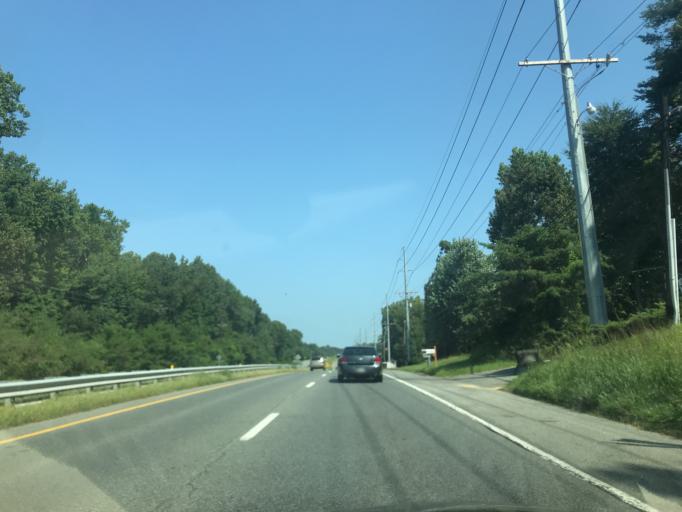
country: US
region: Maryland
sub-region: Calvert County
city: Huntingtown Town Center
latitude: 38.6363
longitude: -76.6052
